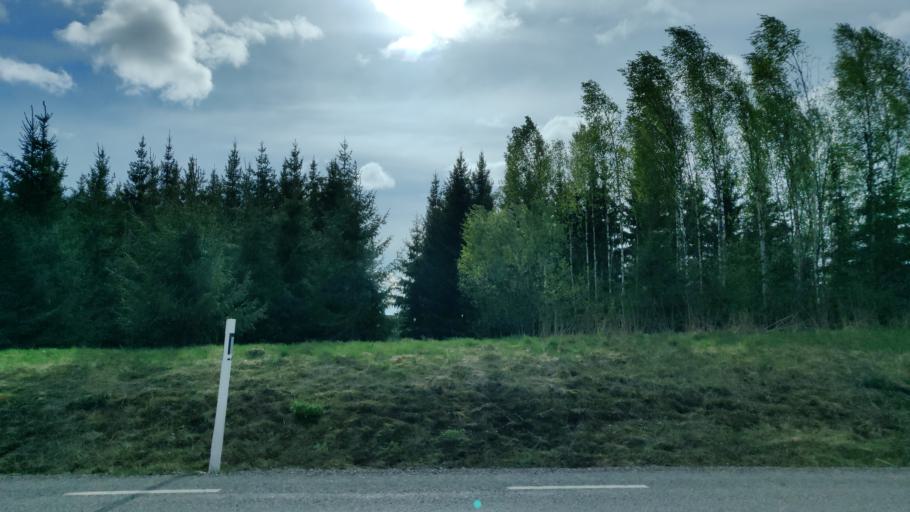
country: SE
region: Vaermland
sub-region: Forshaga Kommun
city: Deje
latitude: 59.5756
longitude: 13.4703
